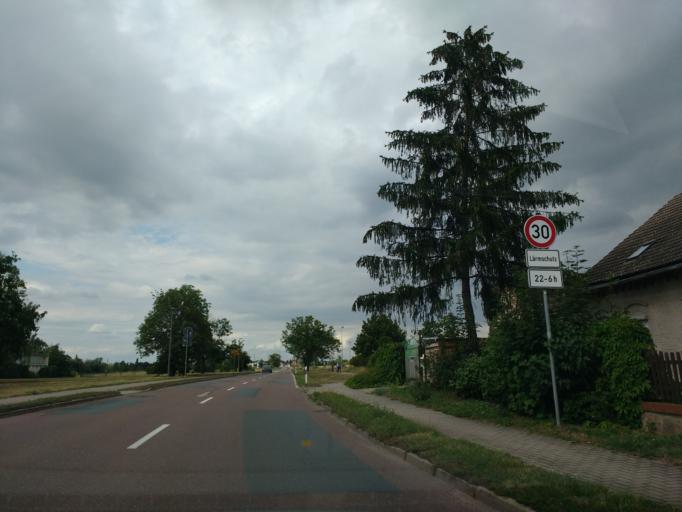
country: DE
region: Saxony-Anhalt
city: Dieskau
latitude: 51.4370
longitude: 12.0406
